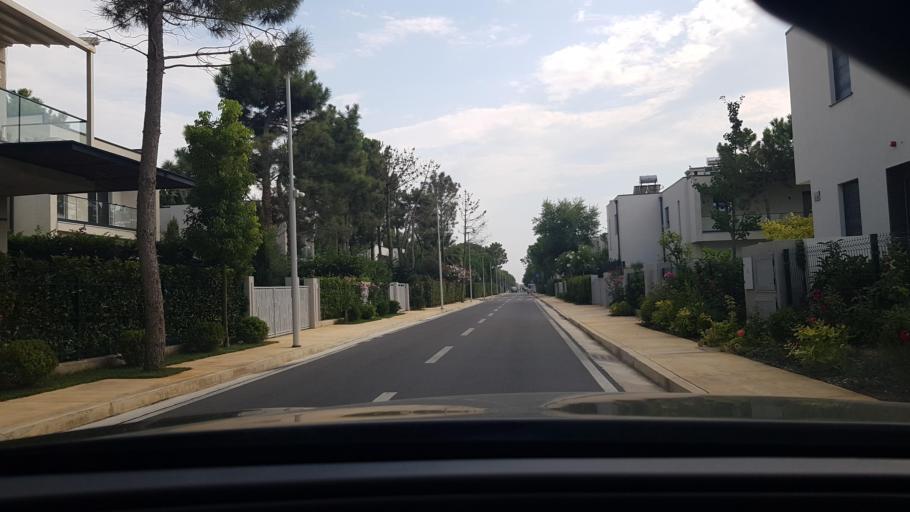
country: AL
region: Durres
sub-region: Rrethi i Durresit
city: Katundi i Ri
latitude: 41.4959
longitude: 19.5141
